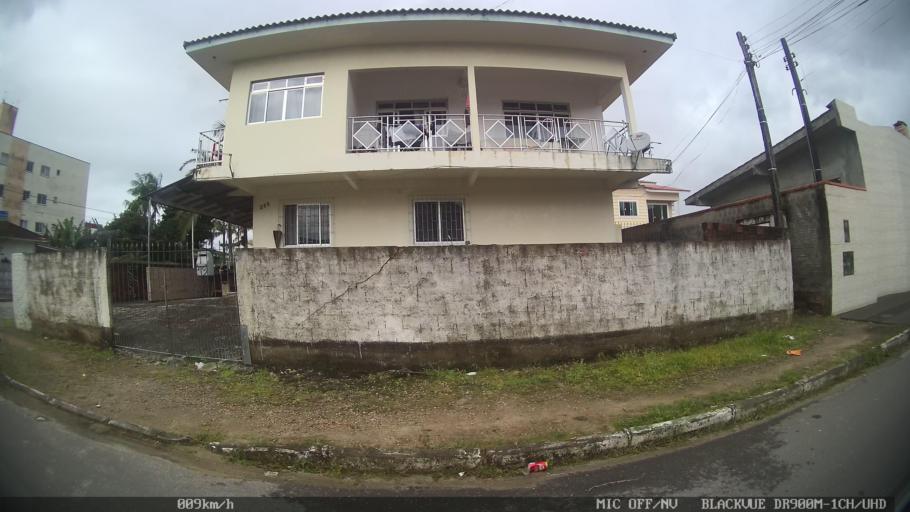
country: BR
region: Santa Catarina
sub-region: Biguacu
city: Biguacu
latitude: -27.5084
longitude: -48.6550
